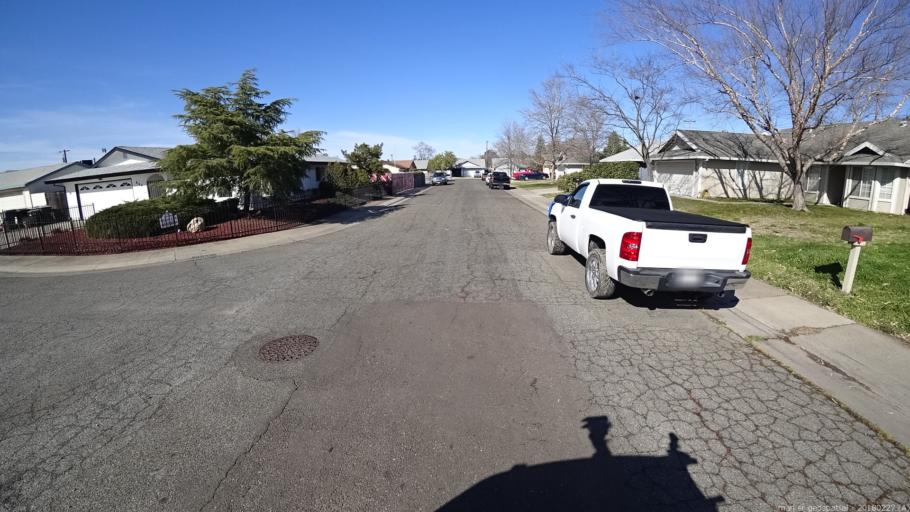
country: US
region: California
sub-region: Sacramento County
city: Rio Linda
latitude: 38.7017
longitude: -121.4458
